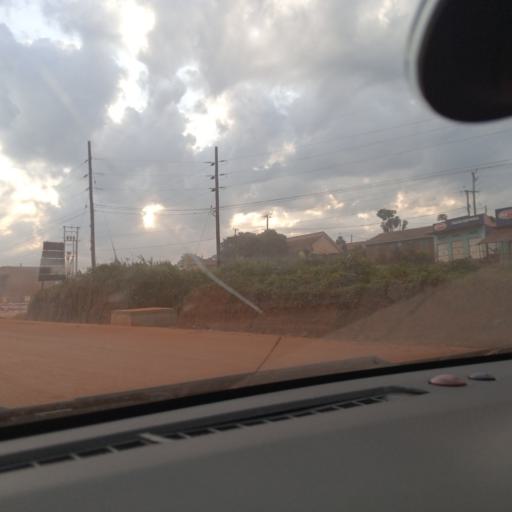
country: UG
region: Central Region
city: Masaka
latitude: -0.3249
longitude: 31.7537
